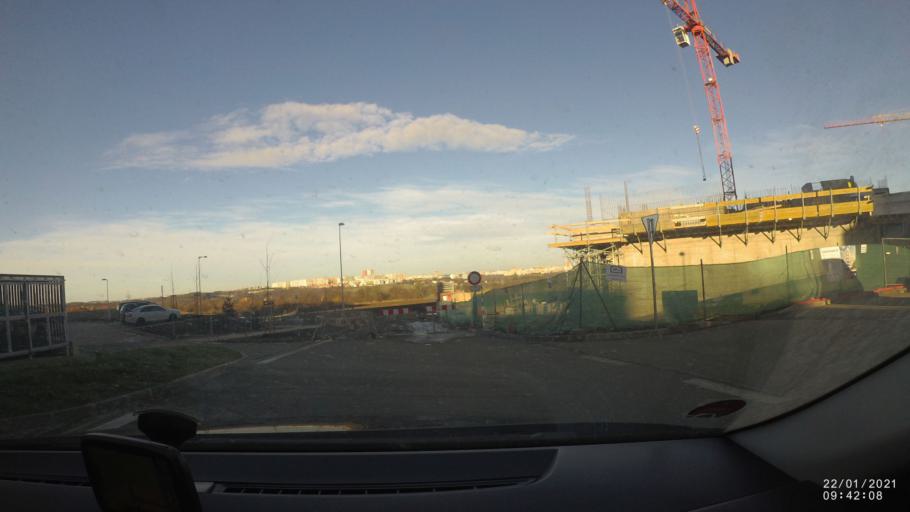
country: CZ
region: Praha
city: Branik
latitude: 50.0293
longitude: 14.3619
